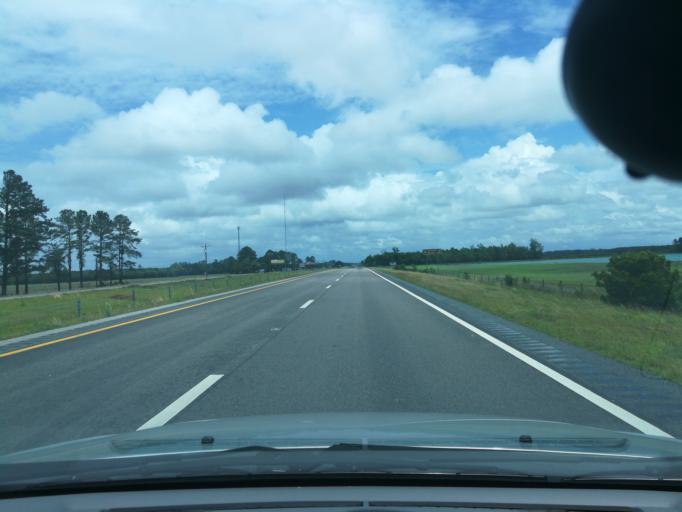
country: US
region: North Carolina
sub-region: Tyrrell County
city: Columbia
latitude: 35.8799
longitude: -76.3750
